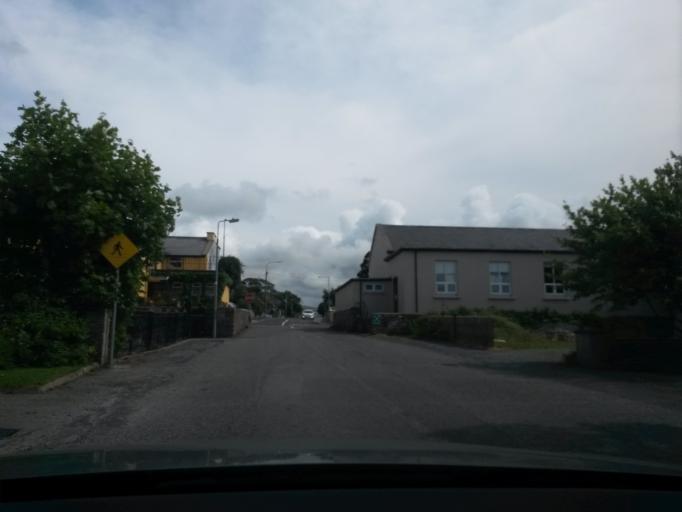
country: IE
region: Connaught
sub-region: Sligo
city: Sligo
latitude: 54.4307
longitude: -8.4544
